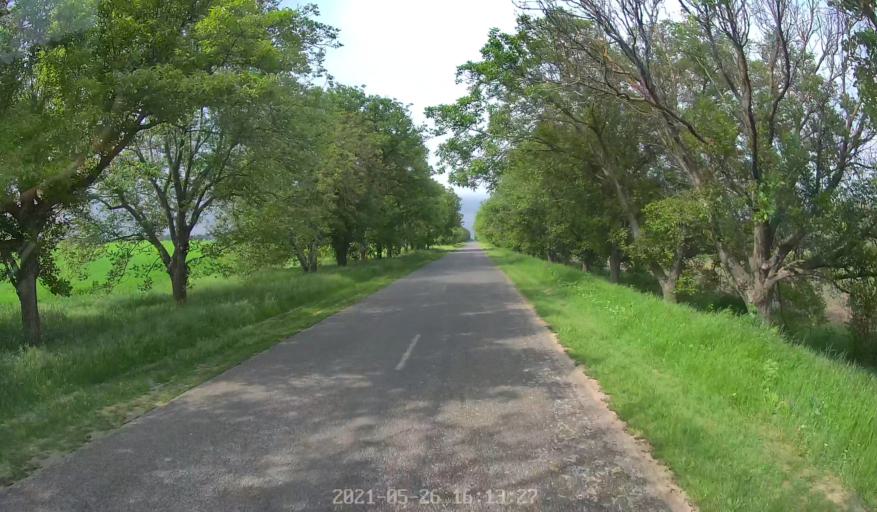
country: MD
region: Hincesti
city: Dancu
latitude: 46.7010
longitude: 28.3379
